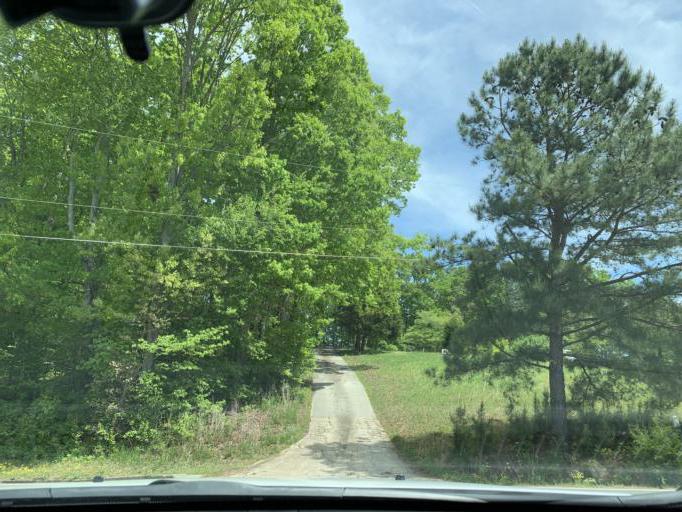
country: US
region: Georgia
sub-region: Hall County
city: Flowery Branch
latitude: 34.2558
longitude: -84.0241
